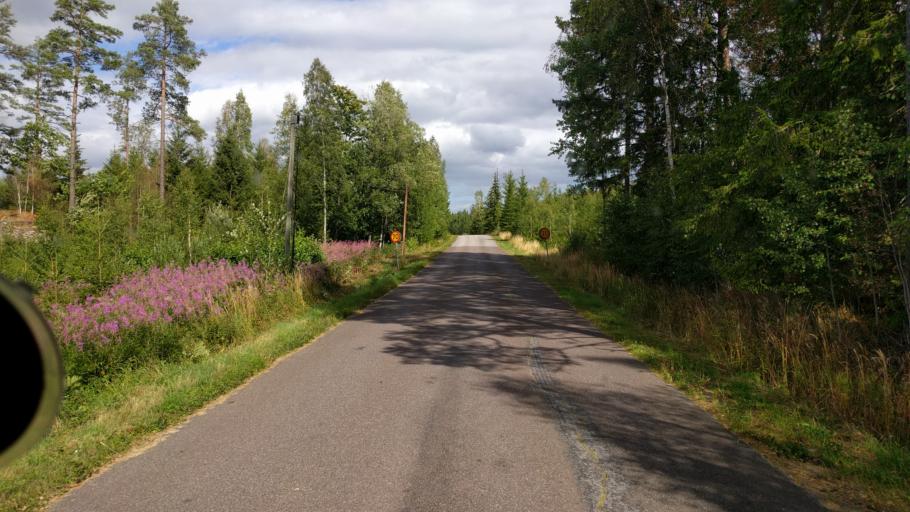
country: SE
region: Kalmar
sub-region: Vimmerby Kommun
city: Vimmerby
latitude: 57.7073
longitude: 16.0178
